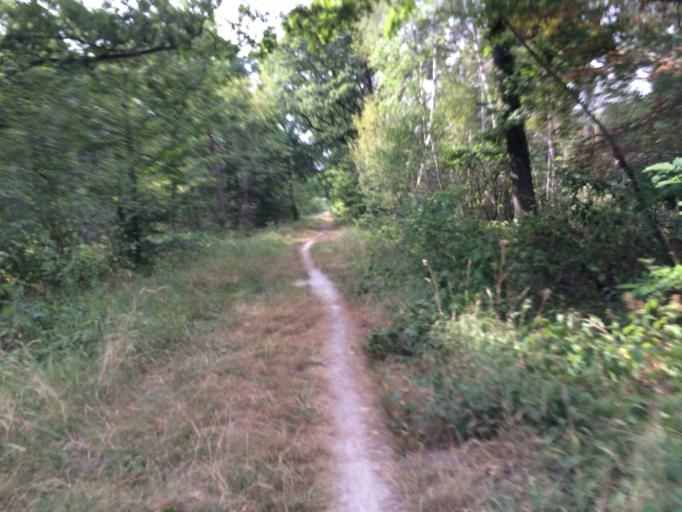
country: FR
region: Ile-de-France
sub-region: Departement de l'Essonne
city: Quincy-sous-Senart
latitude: 48.6730
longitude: 2.5200
